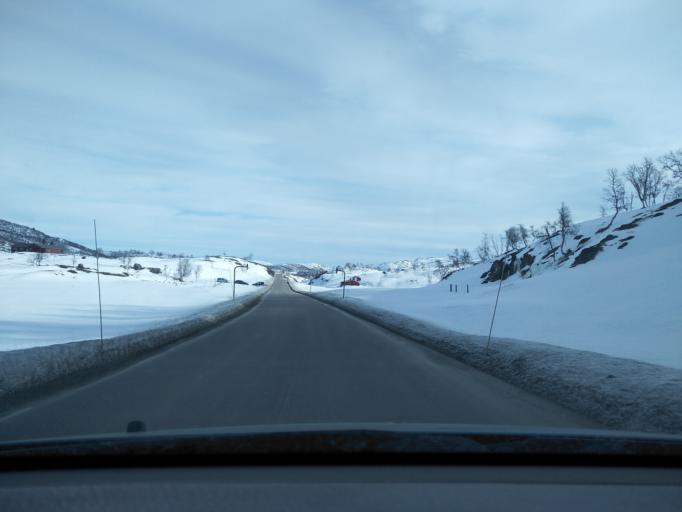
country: NO
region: Aust-Agder
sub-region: Bykle
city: Hovden
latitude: 59.6589
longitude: 7.5055
